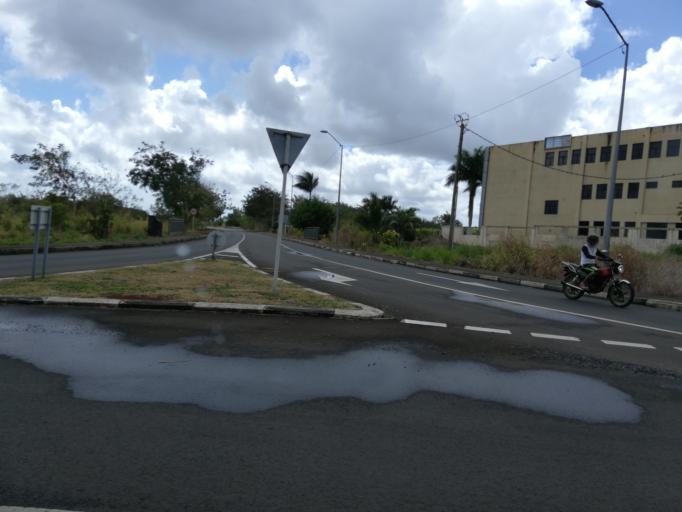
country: MU
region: Pamplemousses
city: Arsenal
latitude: -20.0892
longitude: 57.5444
